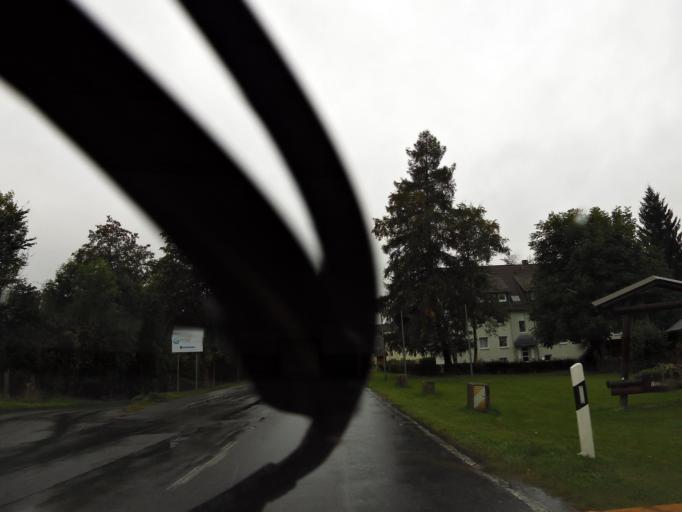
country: DE
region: Lower Saxony
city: Herzberg am Harz
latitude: 51.6255
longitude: 10.3944
